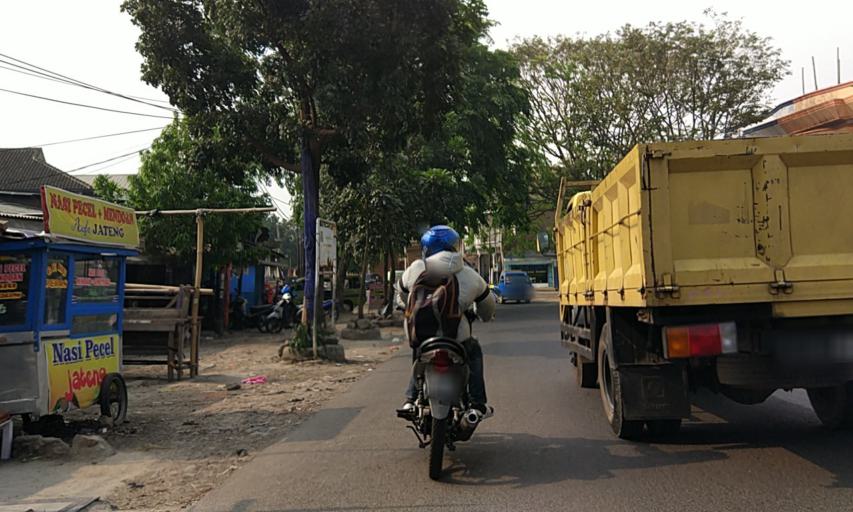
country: ID
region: West Java
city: Margahayukencana
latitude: -6.9509
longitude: 107.5650
